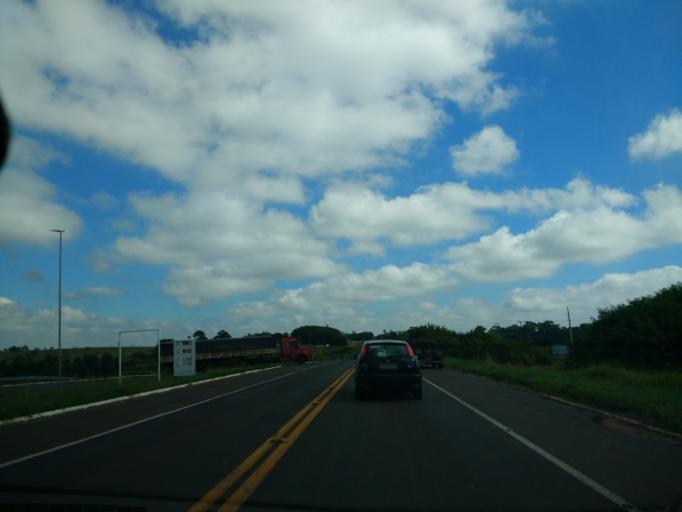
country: BR
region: Parana
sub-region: Cruzeiro Do Oeste
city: Cruzeiro do Oeste
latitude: -23.7649
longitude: -53.1312
